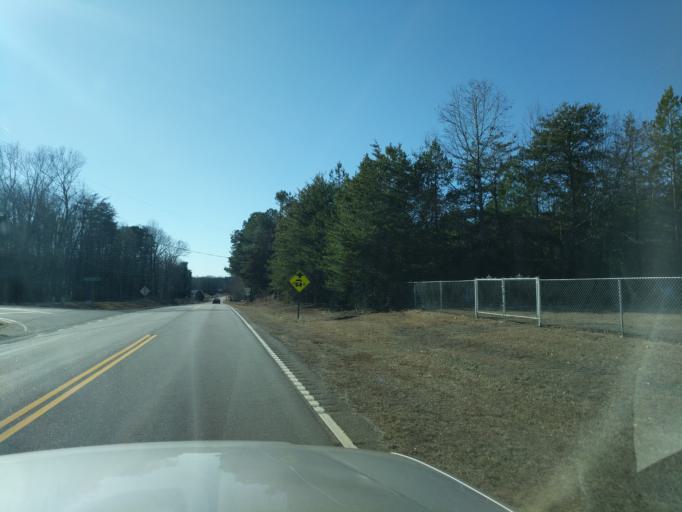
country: US
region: South Carolina
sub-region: Anderson County
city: Homeland Park
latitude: 34.4446
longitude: -82.7173
